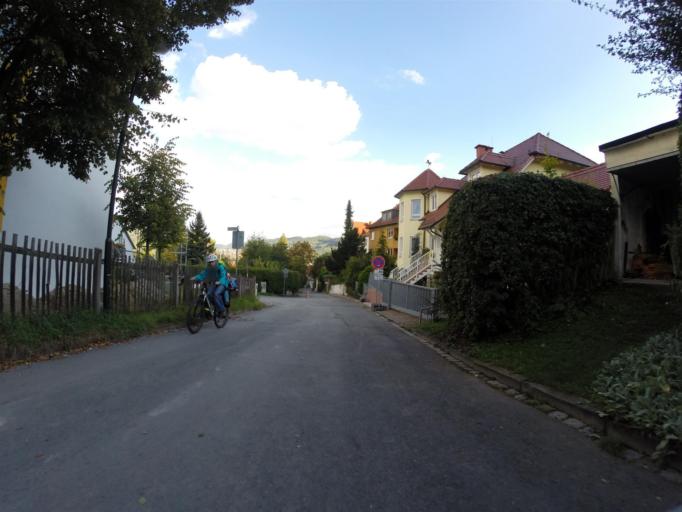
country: DE
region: Thuringia
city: Jena
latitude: 50.9376
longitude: 11.5834
